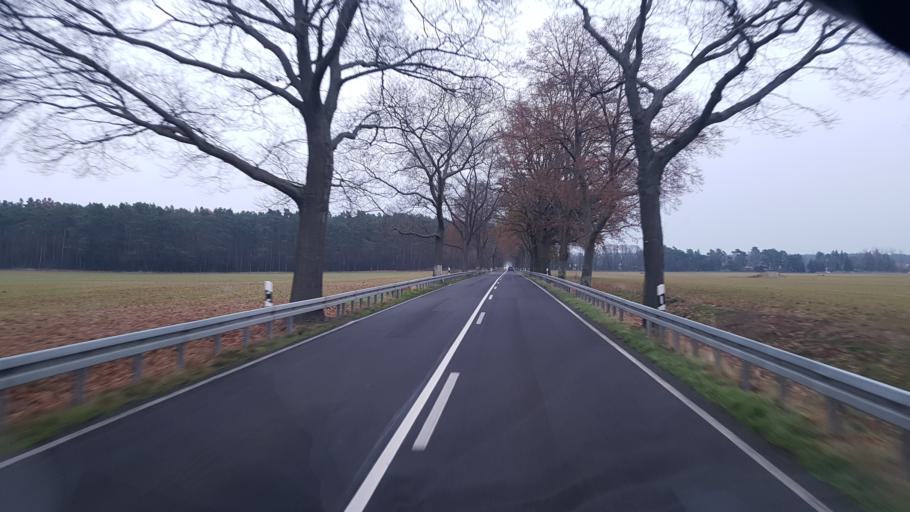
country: DE
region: Brandenburg
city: Janschwalde
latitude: 51.9336
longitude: 14.5443
